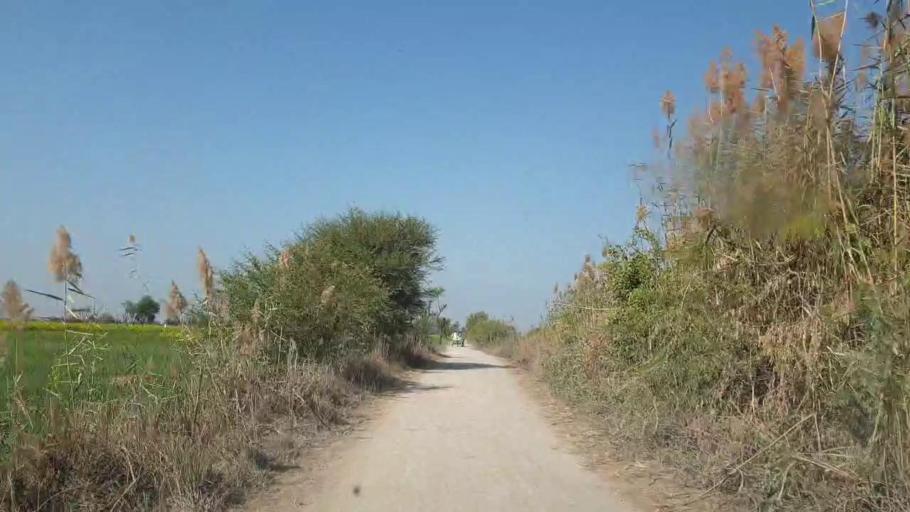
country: PK
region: Sindh
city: Mirpur Khas
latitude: 25.7210
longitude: 69.1393
